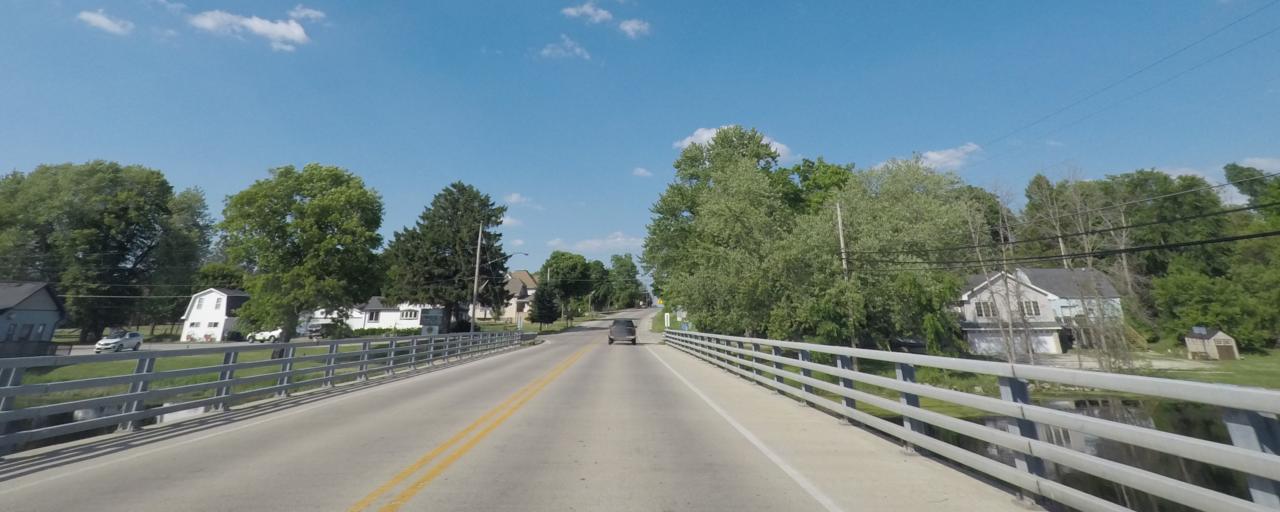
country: US
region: Wisconsin
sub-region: Waukesha County
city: Big Bend
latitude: 42.8760
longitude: -88.2110
